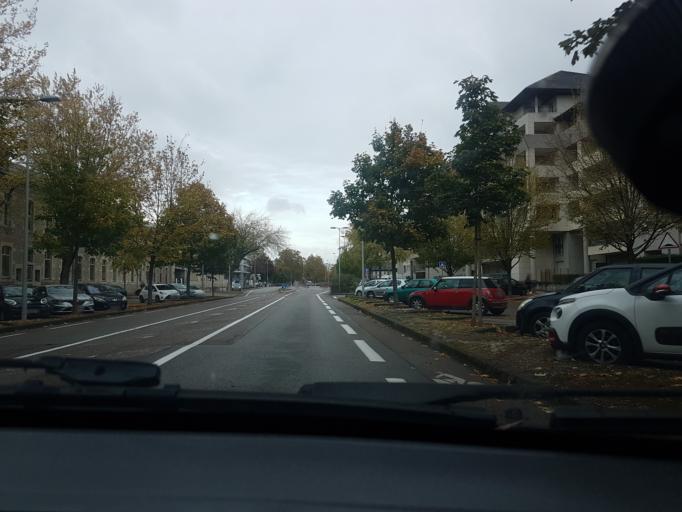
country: FR
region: Bourgogne
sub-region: Departement de la Cote-d'Or
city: Longvic
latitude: 47.3171
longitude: 5.0513
